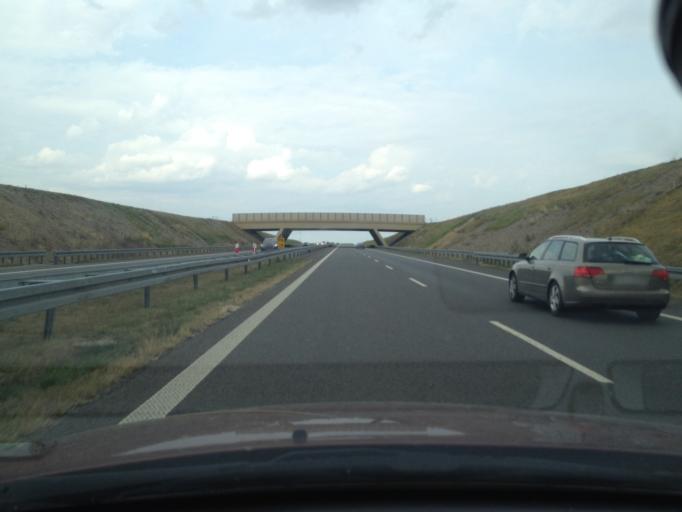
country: PL
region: West Pomeranian Voivodeship
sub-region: Powiat pyrzycki
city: Kozielice
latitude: 53.0652
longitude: 14.8625
